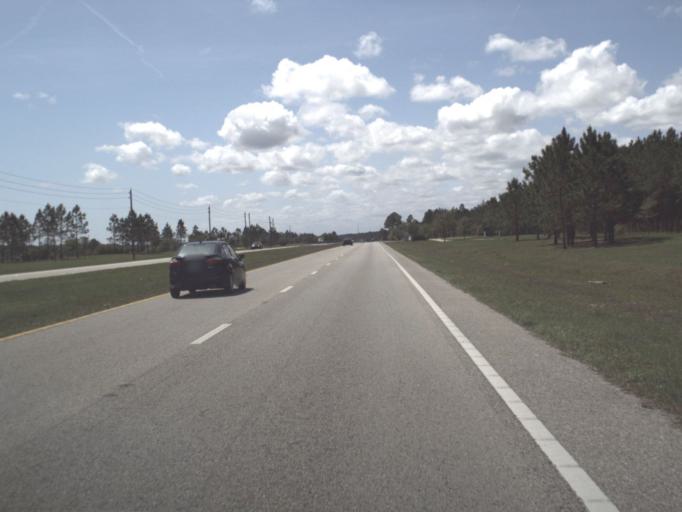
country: US
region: Florida
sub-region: Flagler County
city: Palm Coast
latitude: 29.5950
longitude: -81.2821
